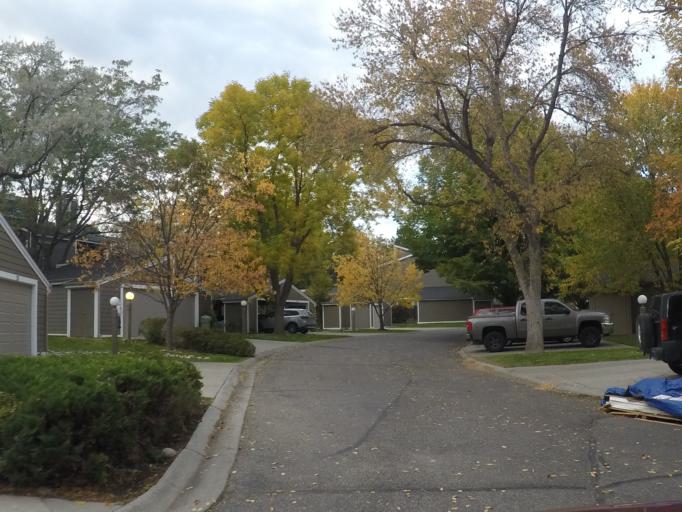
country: US
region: Montana
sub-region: Yellowstone County
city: Billings
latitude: 45.7924
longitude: -108.5559
